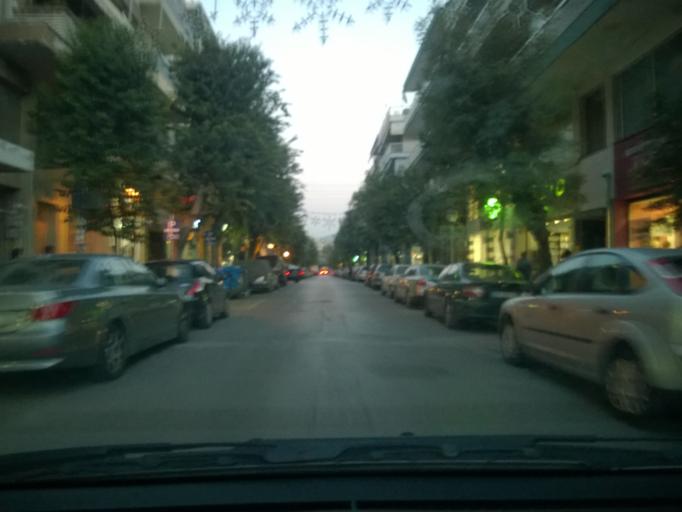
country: GR
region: Central Macedonia
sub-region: Nomos Thessalonikis
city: Ampelokipoi
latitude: 40.6519
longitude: 22.9249
